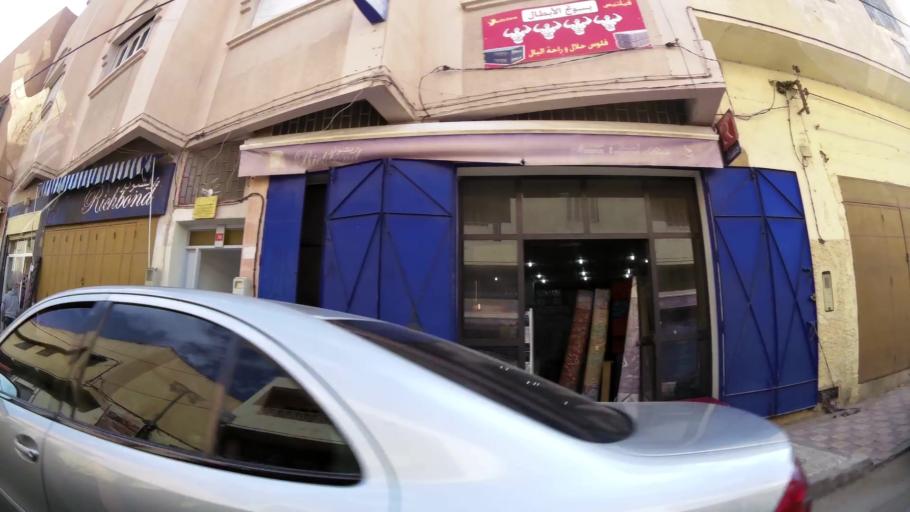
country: MA
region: Oriental
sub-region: Oujda-Angad
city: Oujda
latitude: 34.6828
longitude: -1.9114
